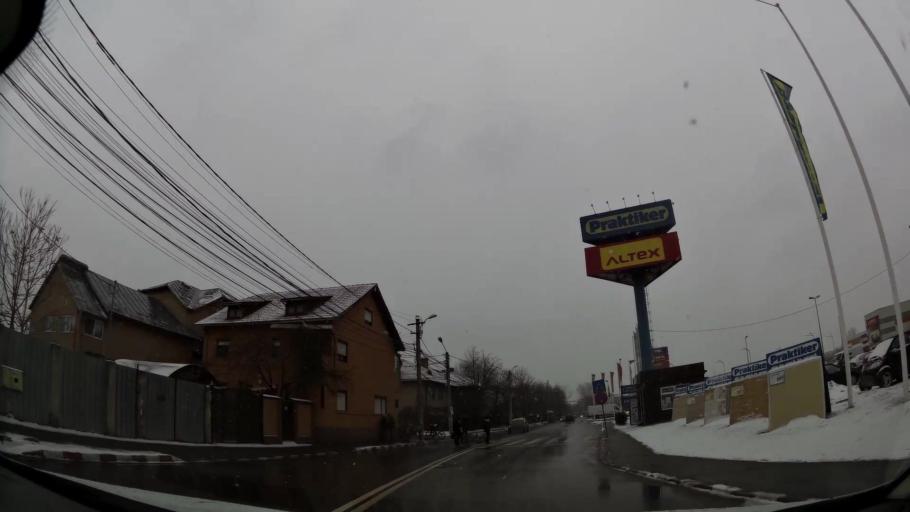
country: RO
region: Dambovita
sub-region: Municipiul Targoviste
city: Targoviste
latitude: 44.9219
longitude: 25.4644
